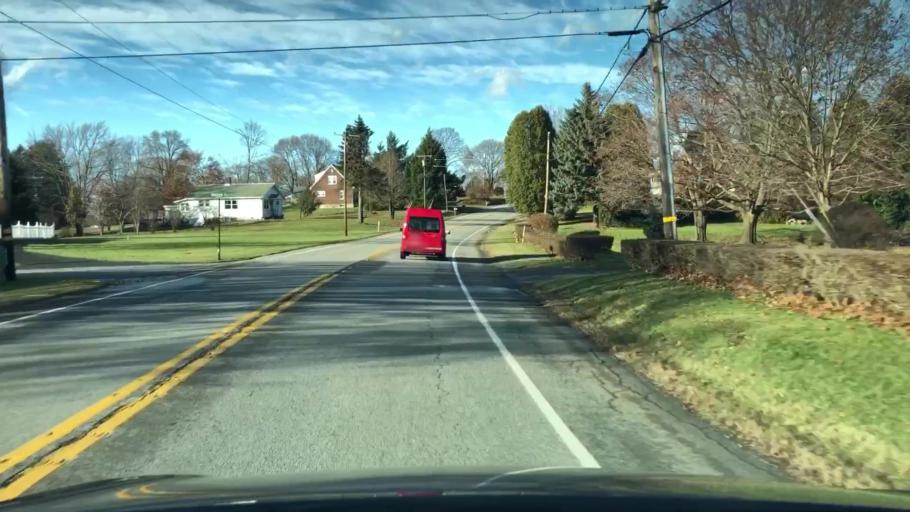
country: US
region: Pennsylvania
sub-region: Butler County
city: Meadowood
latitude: 40.8350
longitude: -79.8677
